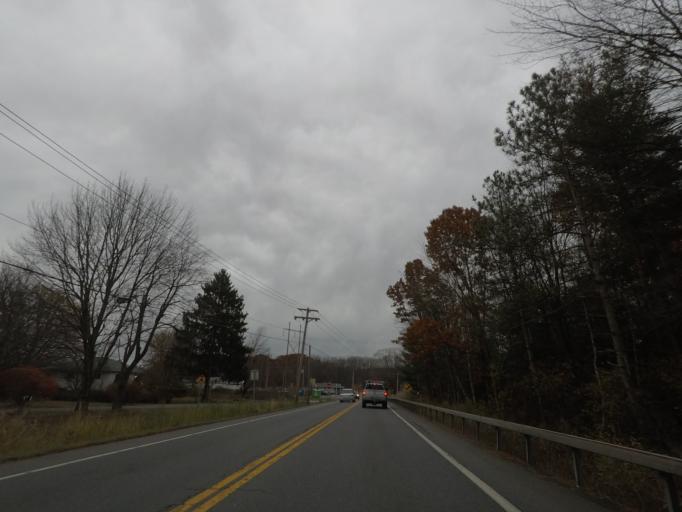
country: US
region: New York
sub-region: Albany County
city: Cohoes
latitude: 42.8200
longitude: -73.7606
